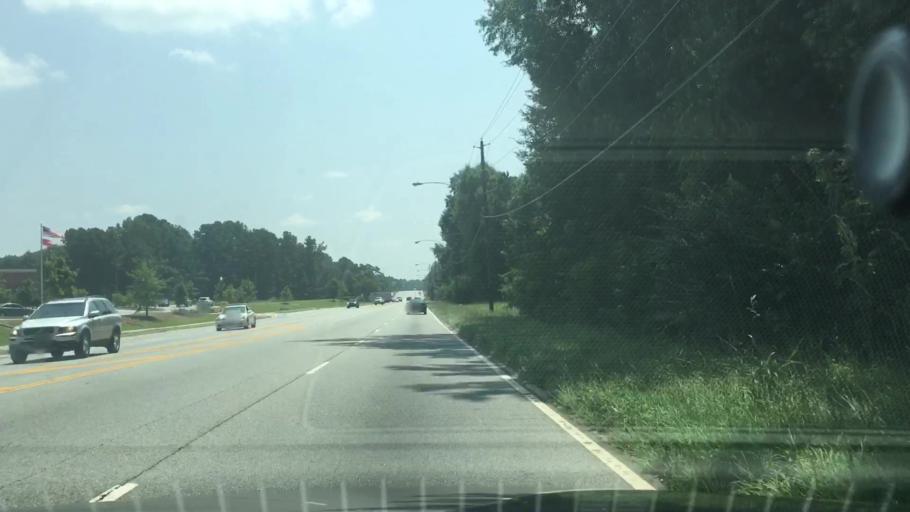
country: US
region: Georgia
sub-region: Spalding County
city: Griffin
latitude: 33.2433
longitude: -84.2506
